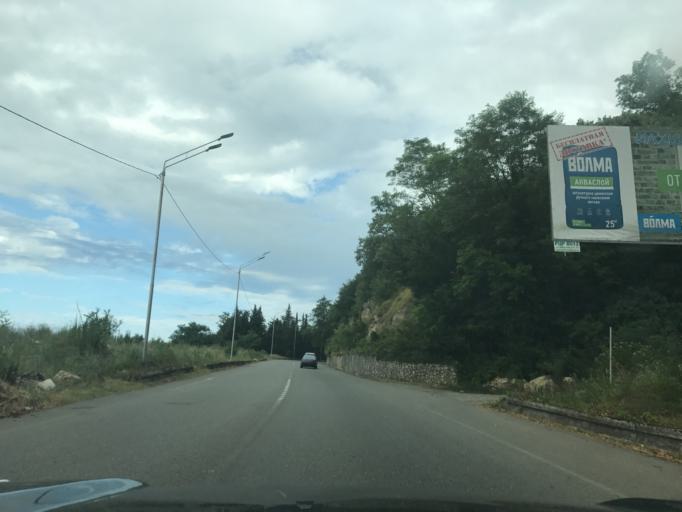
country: GE
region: Abkhazia
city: Gagra
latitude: 43.2807
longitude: 40.2790
